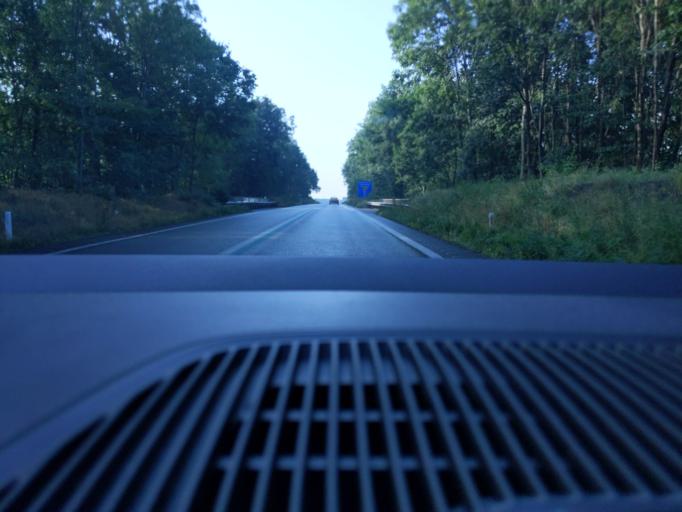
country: NL
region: Drenthe
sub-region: Gemeente Emmen
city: Emmer-Compascuum
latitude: 52.9168
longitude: 7.0371
